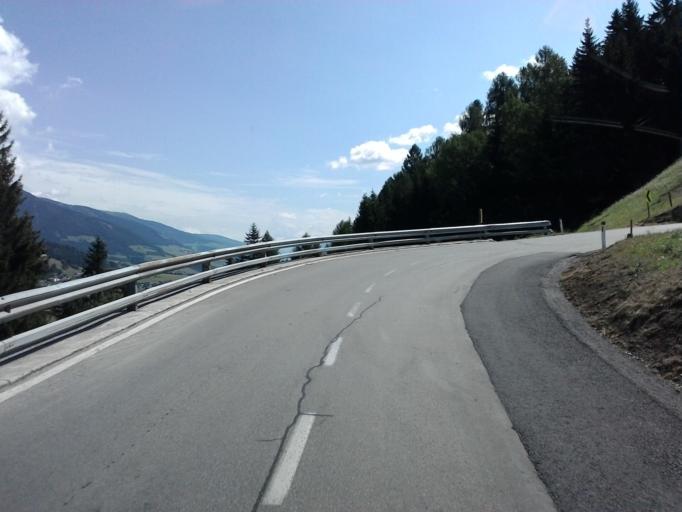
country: AT
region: Tyrol
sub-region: Politischer Bezirk Lienz
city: Strassen
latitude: 46.7412
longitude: 12.4706
